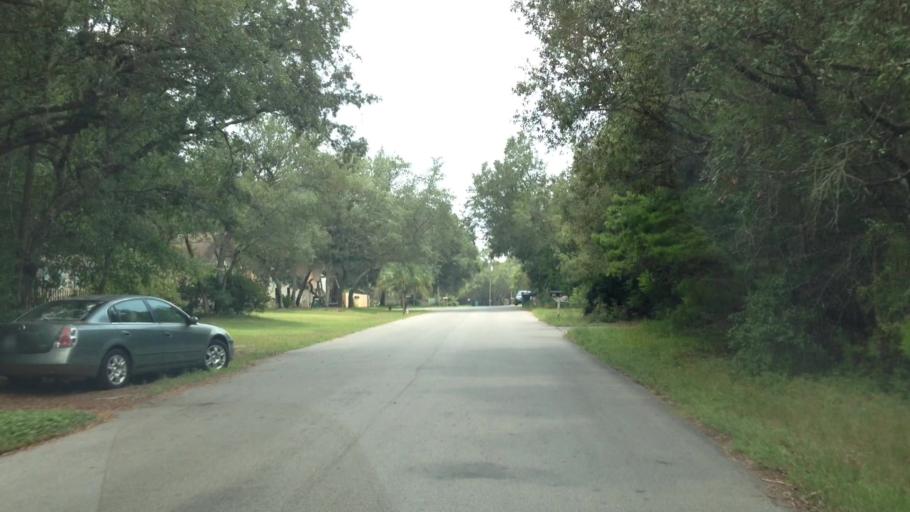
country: US
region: Florida
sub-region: Santa Rosa County
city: Holley
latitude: 30.4349
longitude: -86.9355
